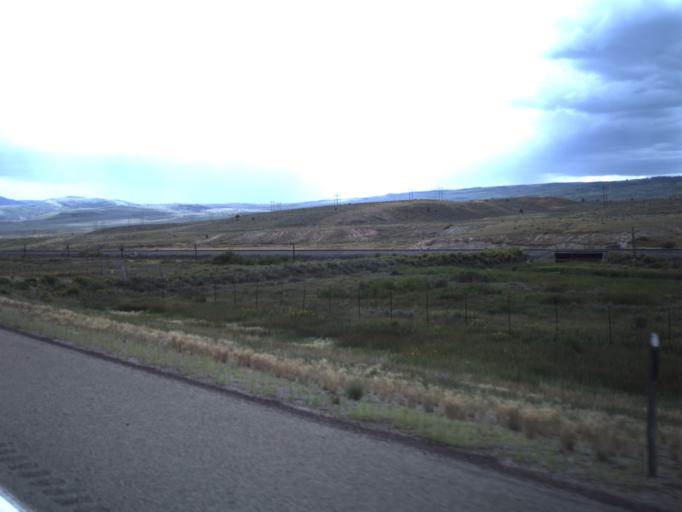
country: US
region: Utah
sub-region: Carbon County
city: Helper
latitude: 39.8741
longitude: -111.0349
